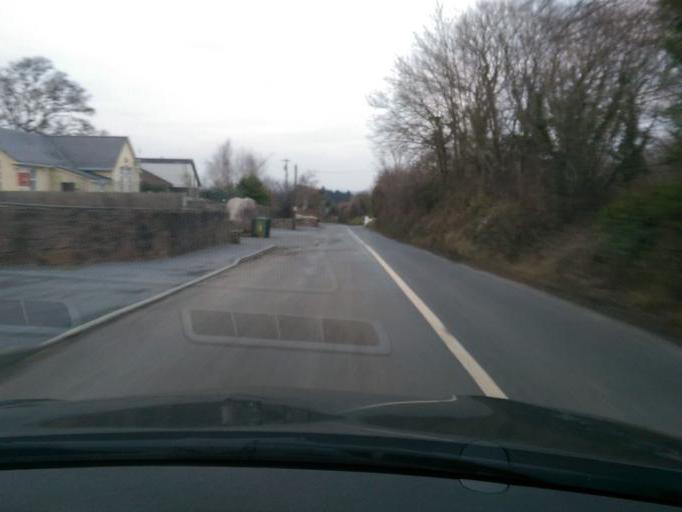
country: IE
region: Connaught
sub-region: County Galway
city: Moycullen
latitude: 53.3065
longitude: -9.1531
